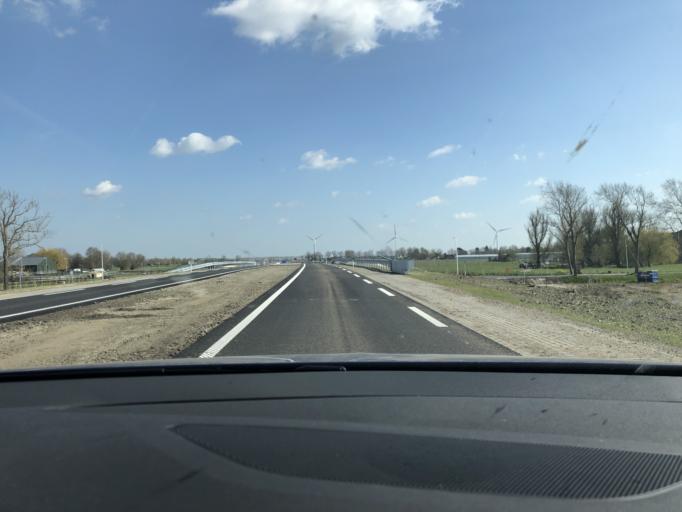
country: NL
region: South Holland
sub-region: Gemeente Waddinxveen
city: Groenswaard
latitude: 52.0342
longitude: 4.6218
